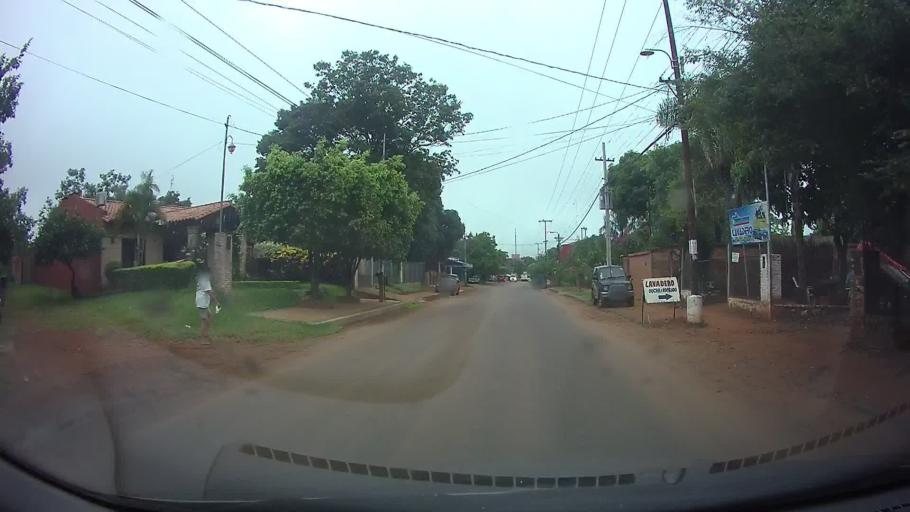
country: PY
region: Central
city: Itaugua
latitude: -25.3886
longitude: -57.3516
